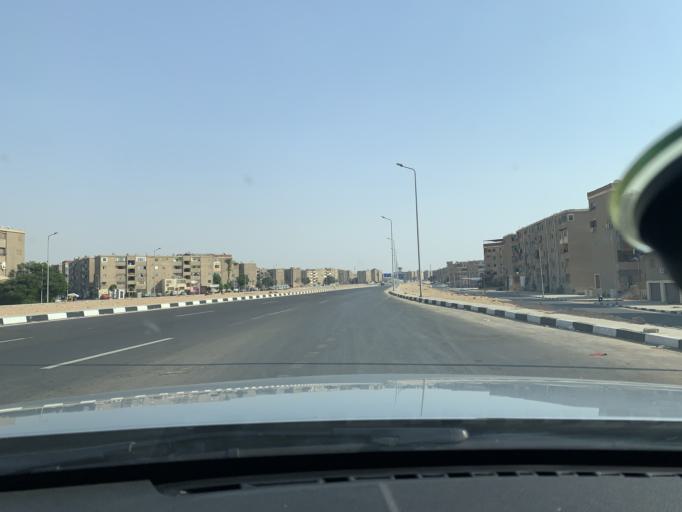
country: EG
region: Muhafazat al Qalyubiyah
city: Al Khankah
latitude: 30.1788
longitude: 31.4148
